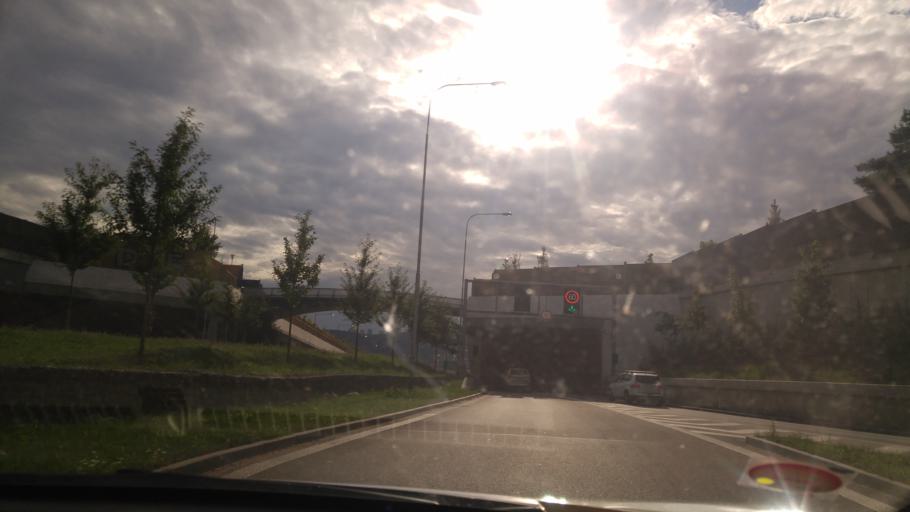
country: CZ
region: South Moravian
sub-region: Mesto Brno
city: Brno
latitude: 49.2172
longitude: 16.5844
